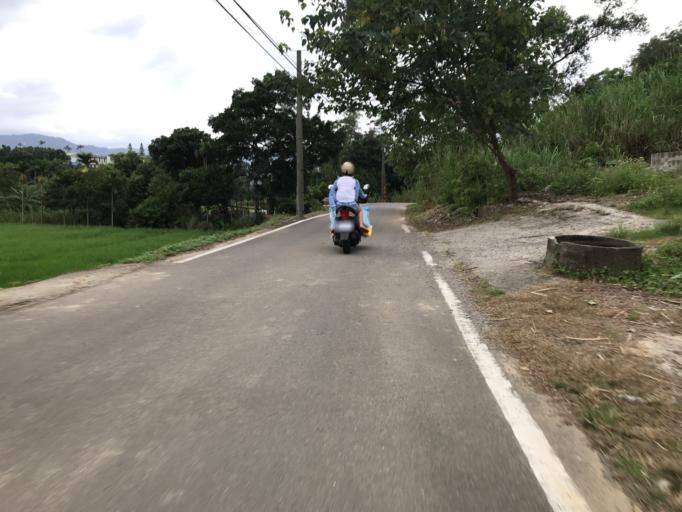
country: TW
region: Taiwan
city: Daxi
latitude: 24.7804
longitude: 121.1747
